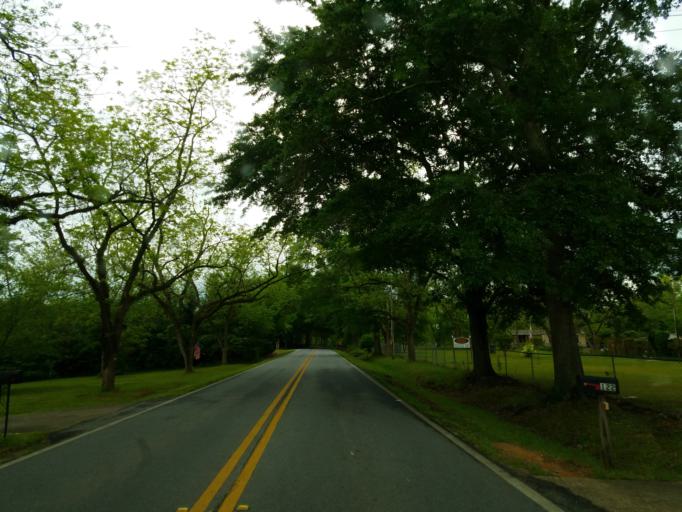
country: US
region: Georgia
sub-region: Lamar County
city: Barnesville
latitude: 33.1085
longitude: -84.1928
